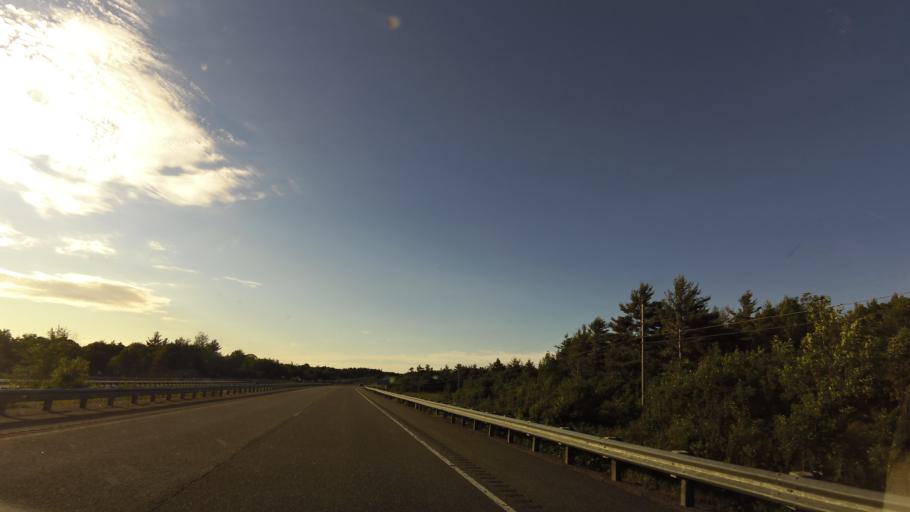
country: CA
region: Ontario
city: Midland
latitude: 44.9059
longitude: -79.7712
